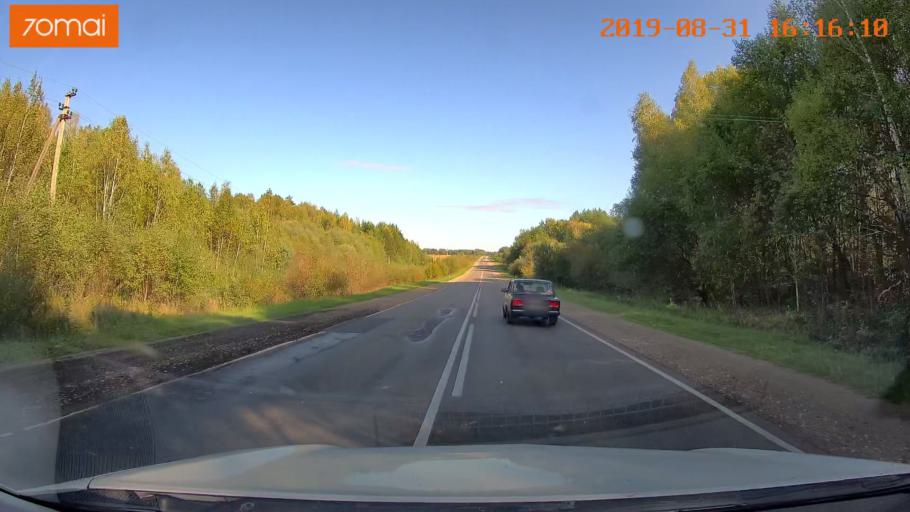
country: RU
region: Kaluga
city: Nikola-Lenivets
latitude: 54.5547
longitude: 35.5041
